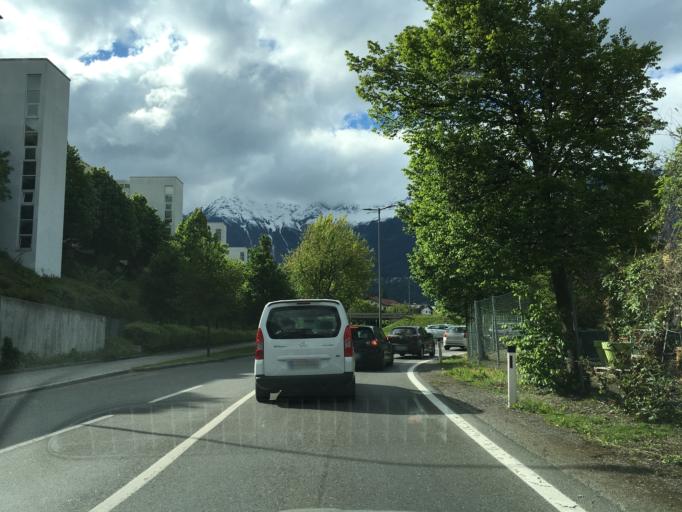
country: AT
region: Tyrol
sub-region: Politischer Bezirk Innsbruck Land
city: Ampass
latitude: 47.2615
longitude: 11.4273
